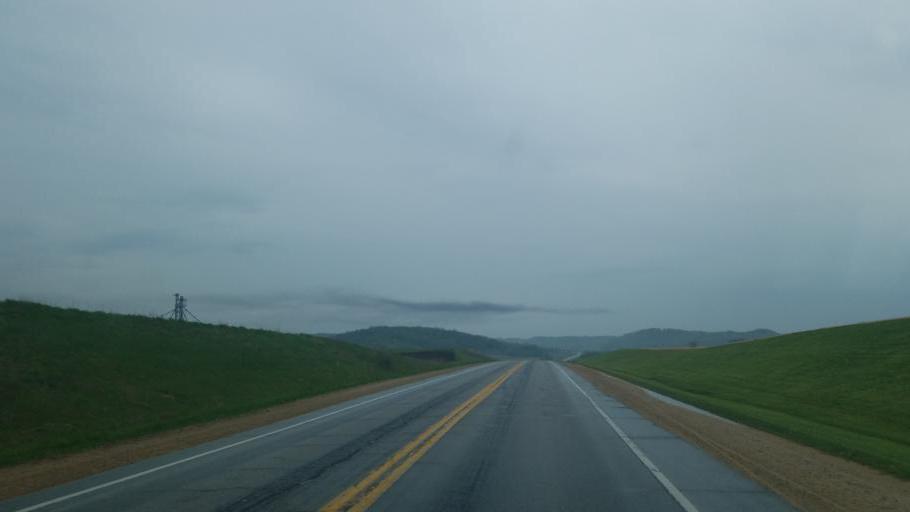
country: US
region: Wisconsin
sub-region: Vernon County
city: Hillsboro
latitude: 43.6433
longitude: -90.3573
